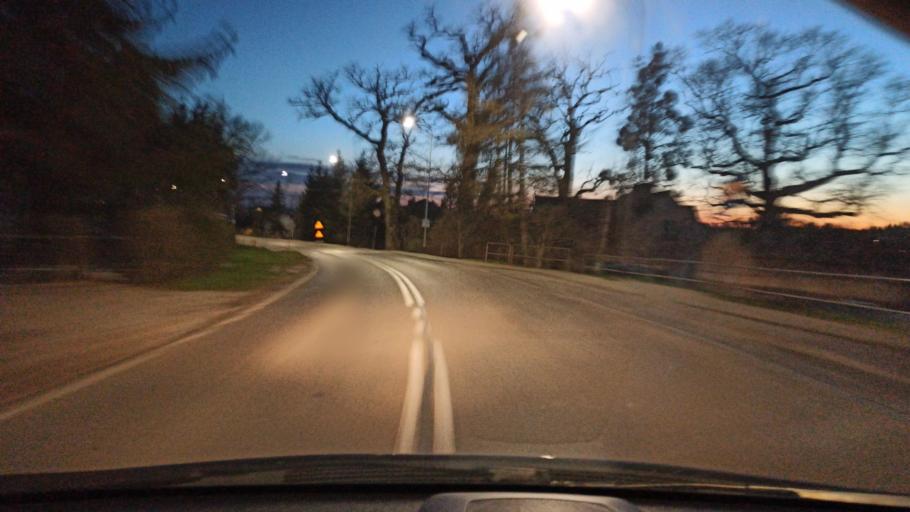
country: PL
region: Warmian-Masurian Voivodeship
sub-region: Powiat elblaski
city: Gronowo Gorne
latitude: 54.1577
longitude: 19.4476
